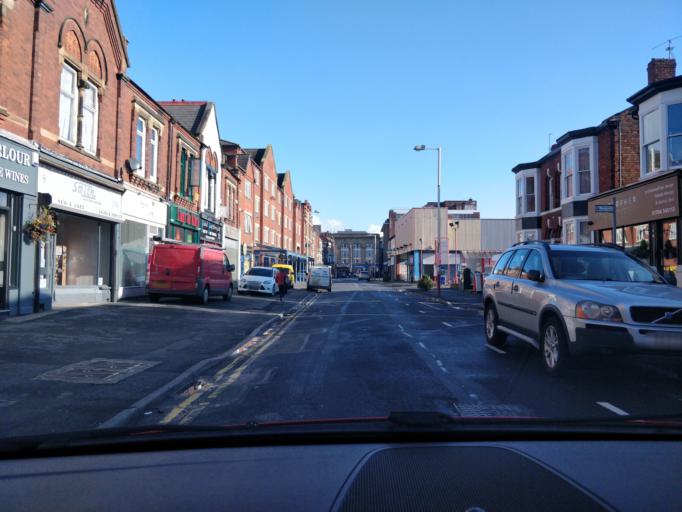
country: GB
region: England
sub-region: Sefton
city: Southport
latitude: 53.6453
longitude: -3.0084
